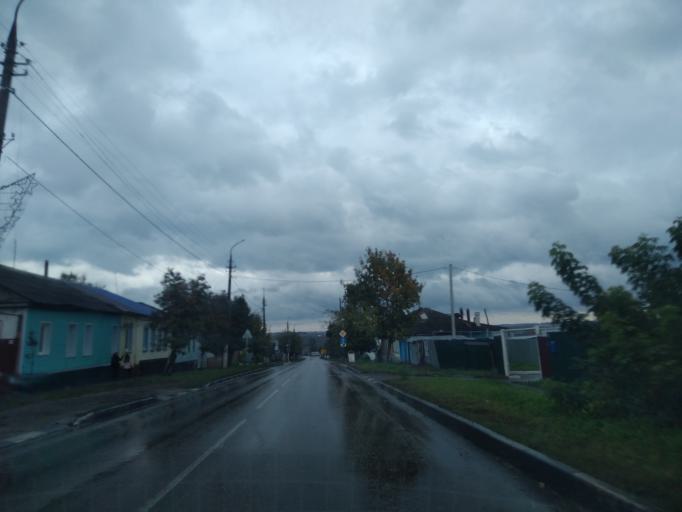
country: RU
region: Tula
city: Yefremov
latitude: 53.1389
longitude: 38.1130
